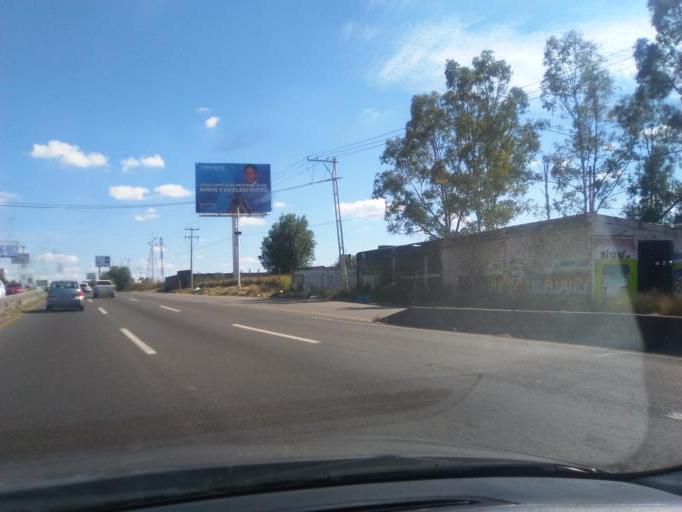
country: MX
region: Guanajuato
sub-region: Silao de la Victoria
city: El Refugio de los Sauces
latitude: 21.0429
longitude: -101.5620
